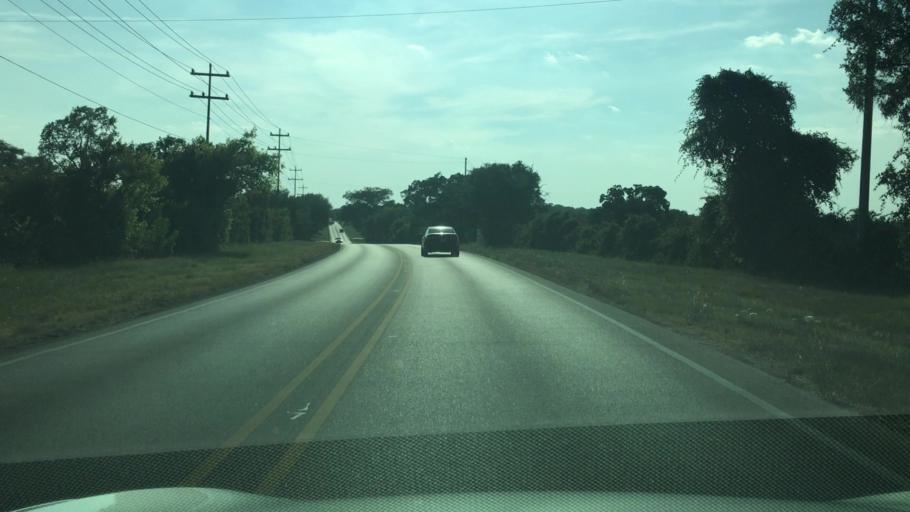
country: US
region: Texas
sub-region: Travis County
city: Shady Hollow
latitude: 30.1173
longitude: -97.9579
